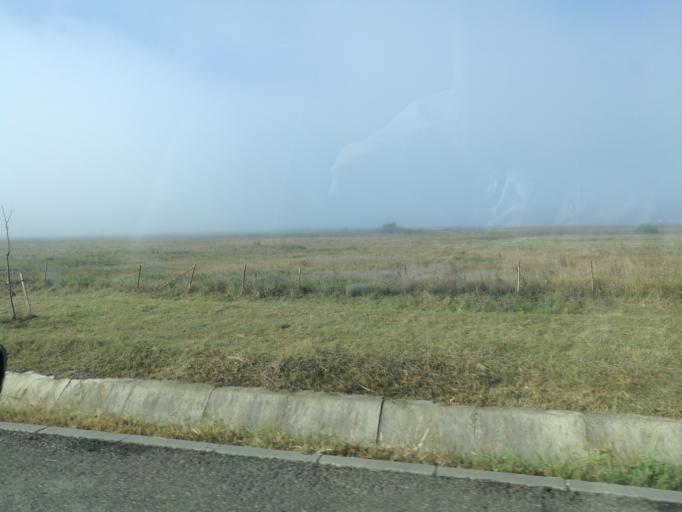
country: RO
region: Iasi
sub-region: Comuna Valea Lupului
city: Valea Lupului
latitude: 47.1692
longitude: 27.5097
